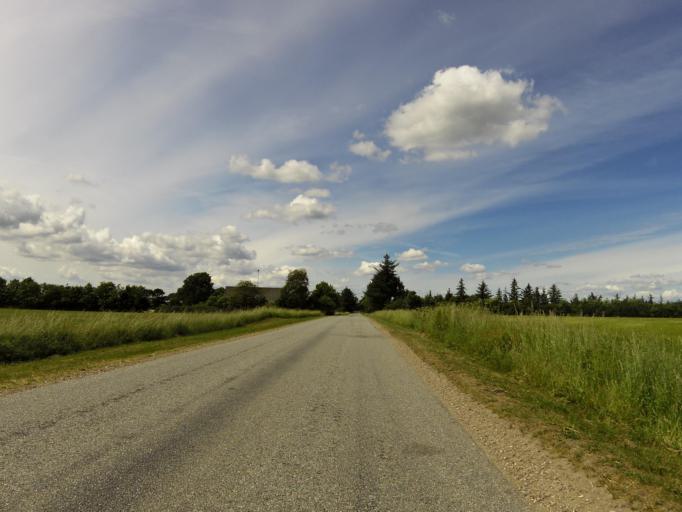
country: DK
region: South Denmark
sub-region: Esbjerg Kommune
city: Ribe
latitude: 55.2618
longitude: 8.8855
